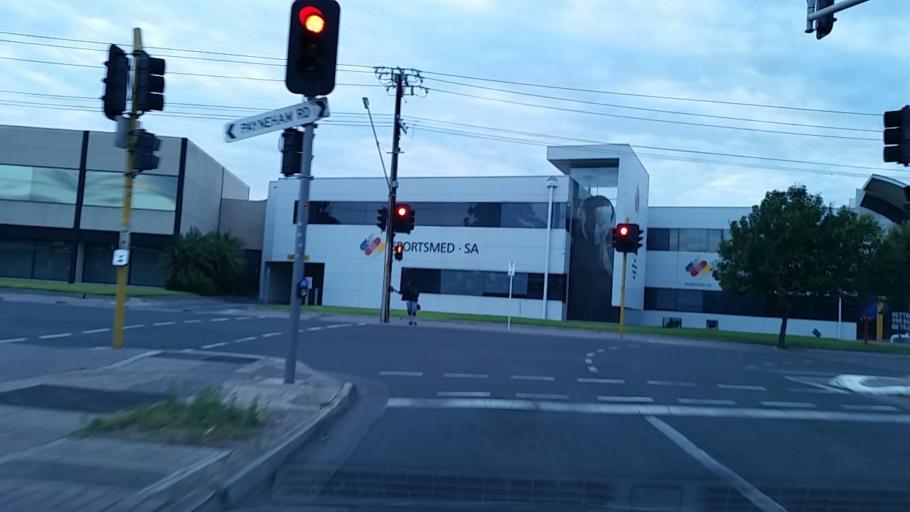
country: AU
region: South Australia
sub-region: Norwood Payneham St Peters
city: Trinity Gardens
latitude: -34.9130
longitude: 138.6246
